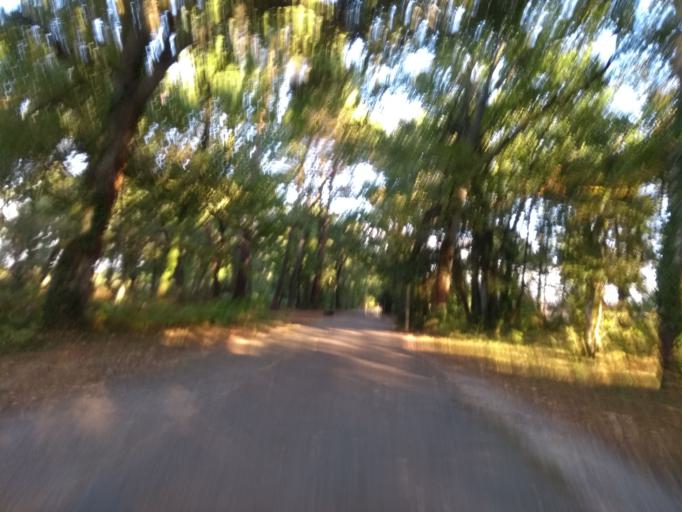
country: FR
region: Aquitaine
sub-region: Departement de la Gironde
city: Pessac
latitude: 44.8052
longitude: -0.6727
